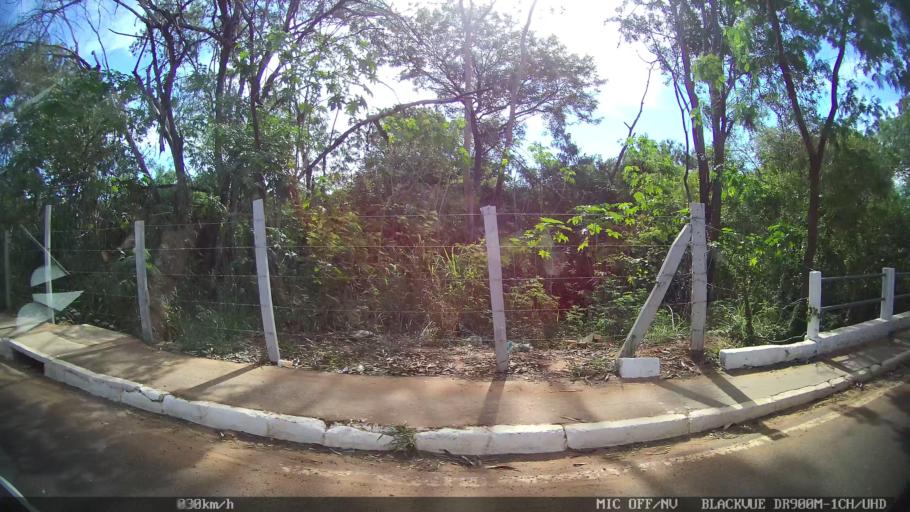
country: BR
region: Sao Paulo
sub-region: Sao Jose Do Rio Preto
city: Sao Jose do Rio Preto
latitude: -20.8429
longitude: -49.3362
